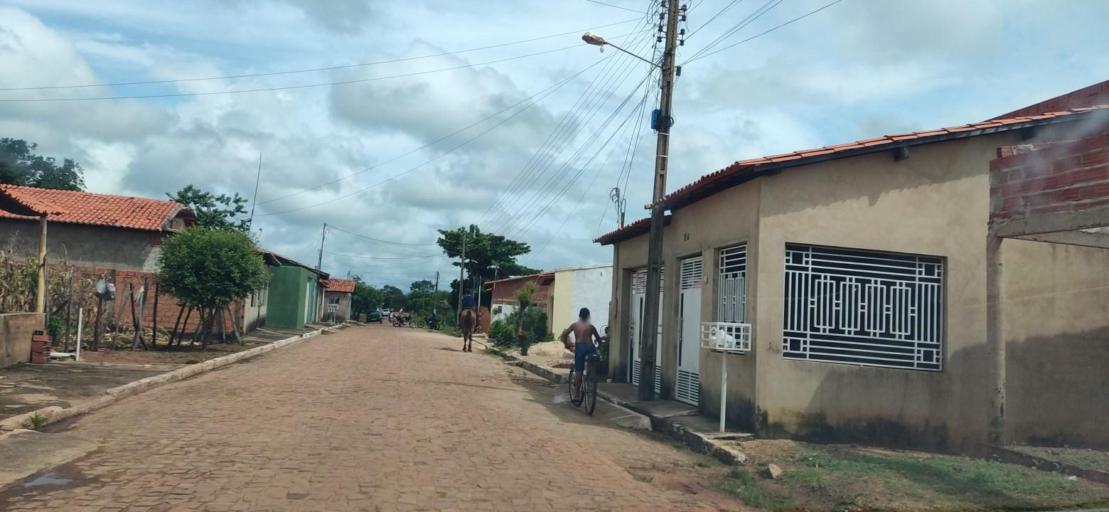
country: BR
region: Piaui
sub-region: Valenca Do Piaui
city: Valenca do Piaui
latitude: -6.1108
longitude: -41.7971
